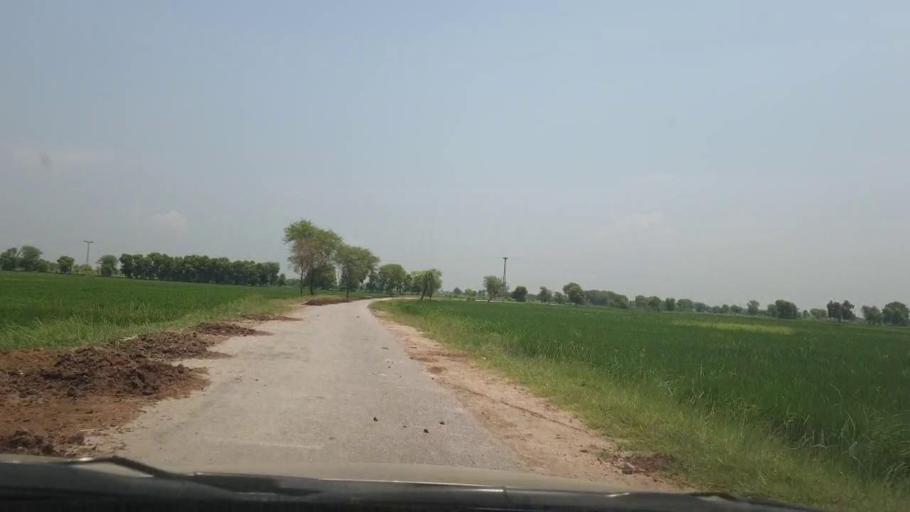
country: PK
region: Sindh
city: Ratodero
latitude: 27.7349
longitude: 68.2998
